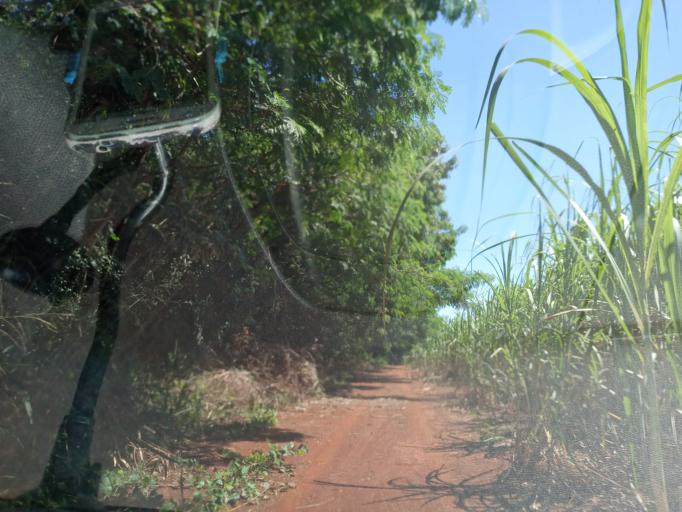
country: BR
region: Goias
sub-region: Itumbiara
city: Itumbiara
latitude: -18.4439
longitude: -49.1415
